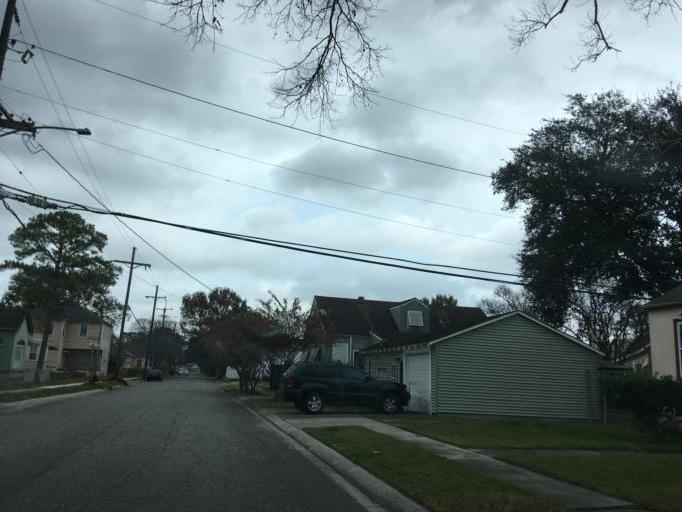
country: US
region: Louisiana
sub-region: Orleans Parish
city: New Orleans
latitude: 29.9961
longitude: -90.0566
